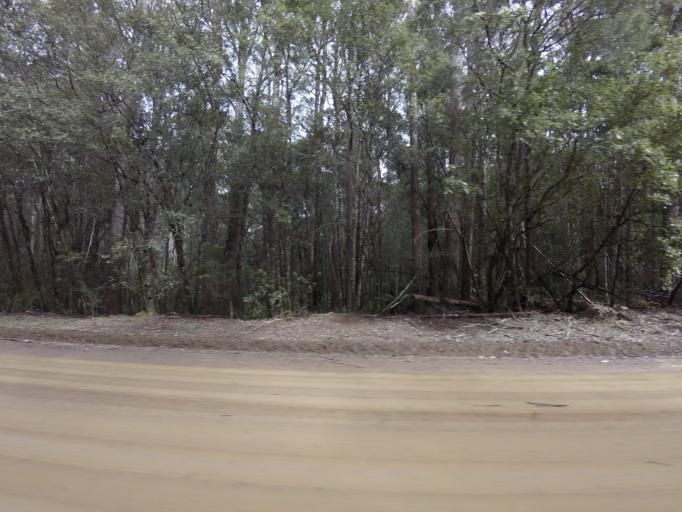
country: AU
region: Tasmania
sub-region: Huon Valley
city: Geeveston
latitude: -43.4116
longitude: 146.8733
